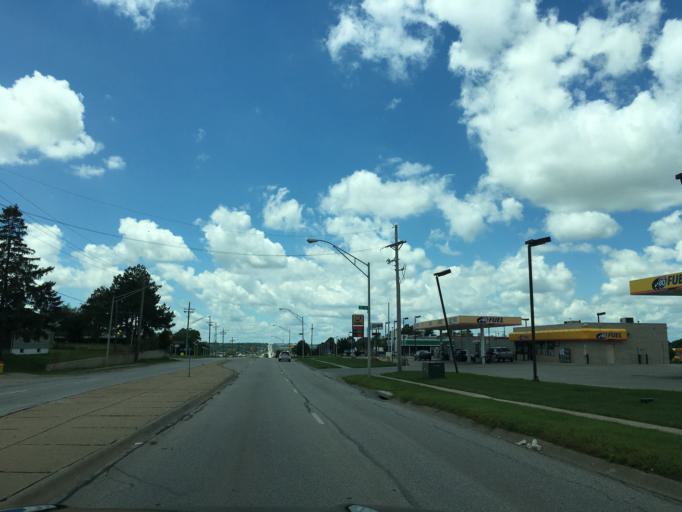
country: US
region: Nebraska
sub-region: Sarpy County
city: La Vista
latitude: 41.2126
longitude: -95.9960
